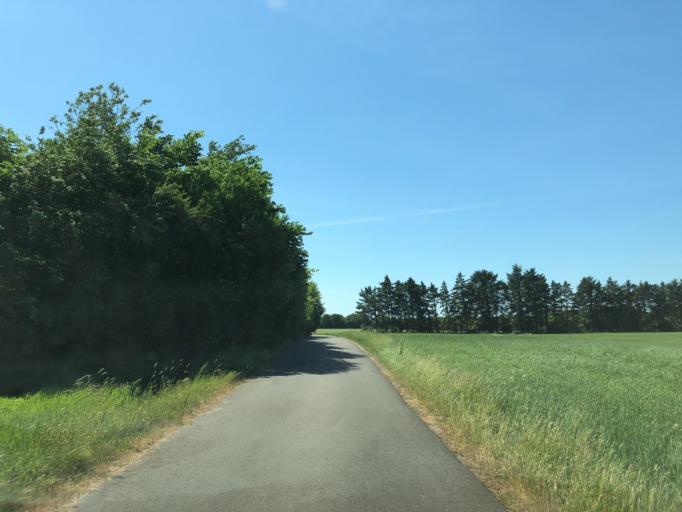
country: DK
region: Central Jutland
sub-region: Struer Kommune
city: Struer
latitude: 56.4302
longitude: 8.4406
